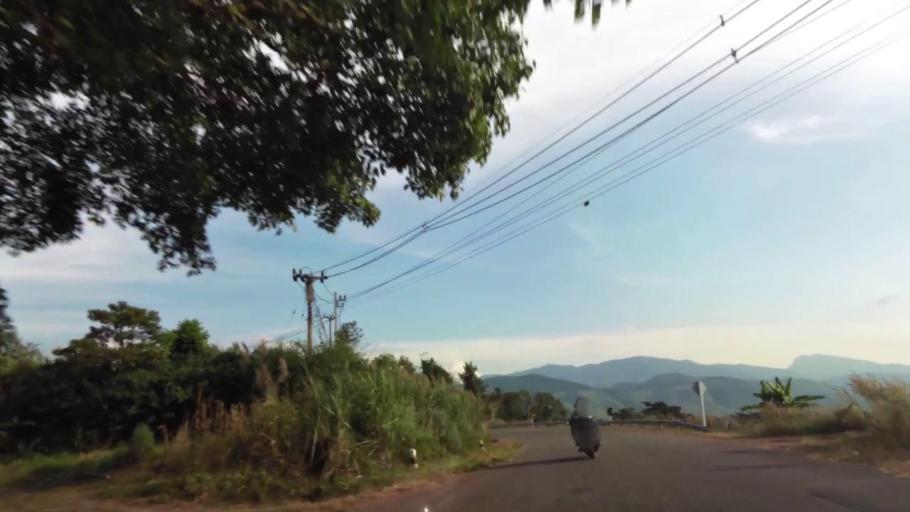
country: TH
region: Chiang Rai
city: Khun Tan
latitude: 19.8532
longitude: 100.3762
